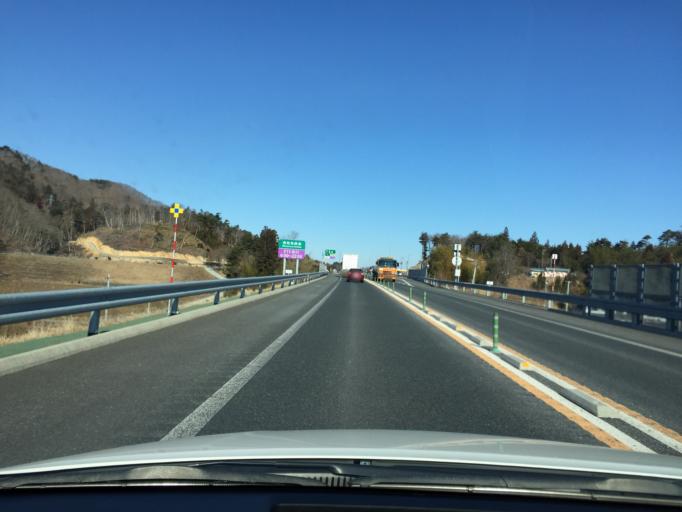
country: JP
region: Fukushima
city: Namie
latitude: 37.7102
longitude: 140.9222
